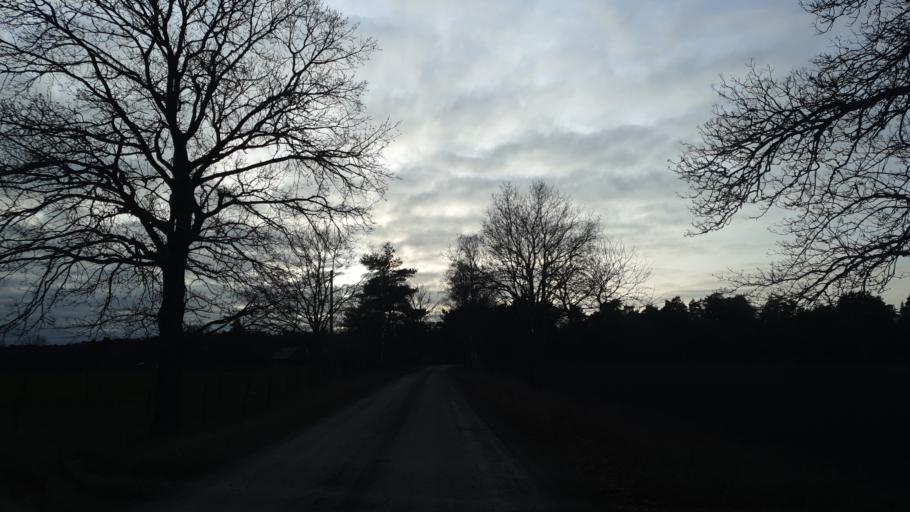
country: SE
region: Kalmar
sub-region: Torsas Kommun
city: Torsas
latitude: 56.3030
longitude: 16.0375
